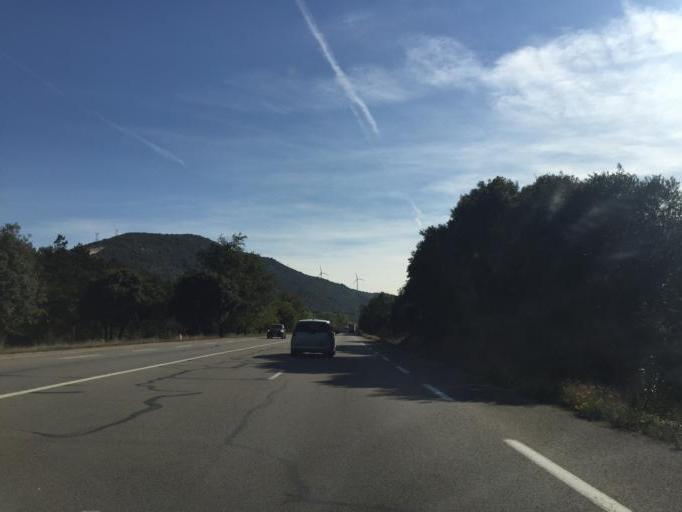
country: FR
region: Rhone-Alpes
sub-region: Departement de la Drome
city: Malataverne
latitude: 44.4782
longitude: 4.7634
